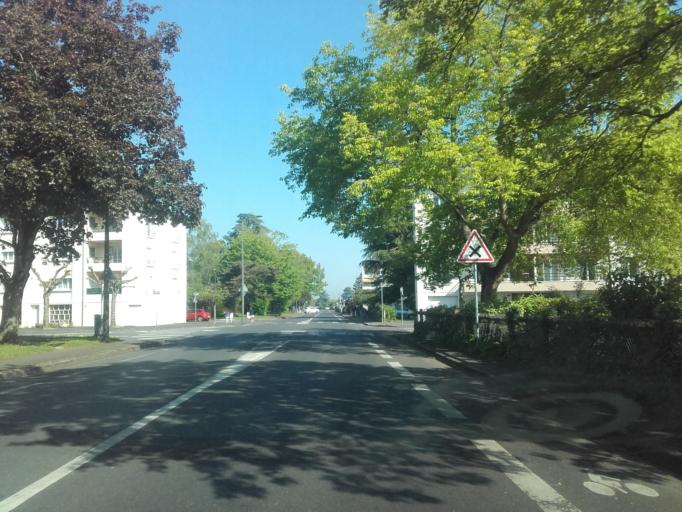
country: FR
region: Centre
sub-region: Departement d'Indre-et-Loire
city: Saint-Cyr-sur-Loire
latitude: 47.4241
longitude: 0.6779
